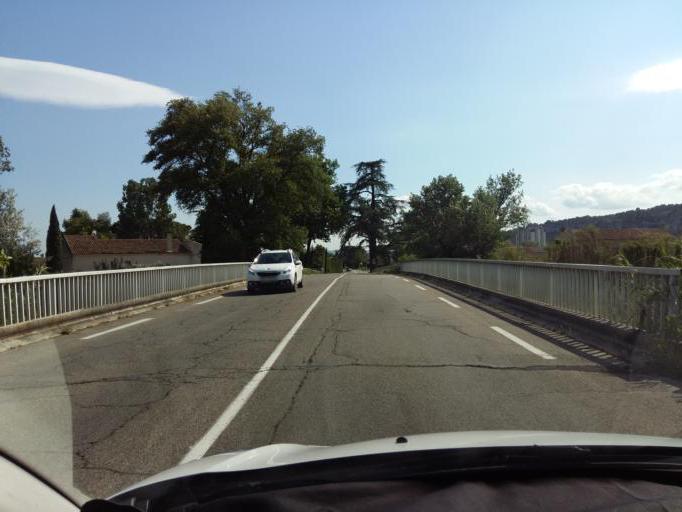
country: FR
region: Provence-Alpes-Cote d'Azur
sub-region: Departement du Vaucluse
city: Cavaillon
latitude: 43.8498
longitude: 5.0489
